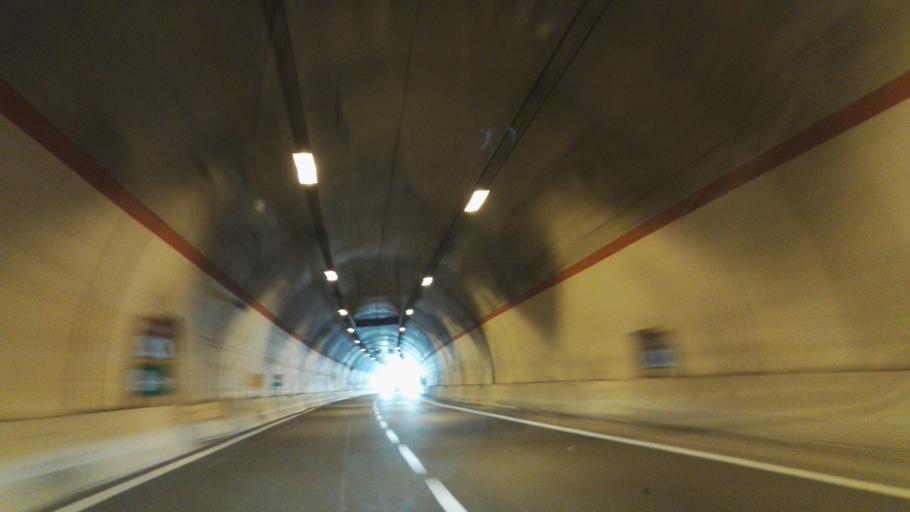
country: IT
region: Calabria
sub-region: Provincia di Catanzaro
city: Squillace Lido
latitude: 38.7927
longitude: 16.5490
